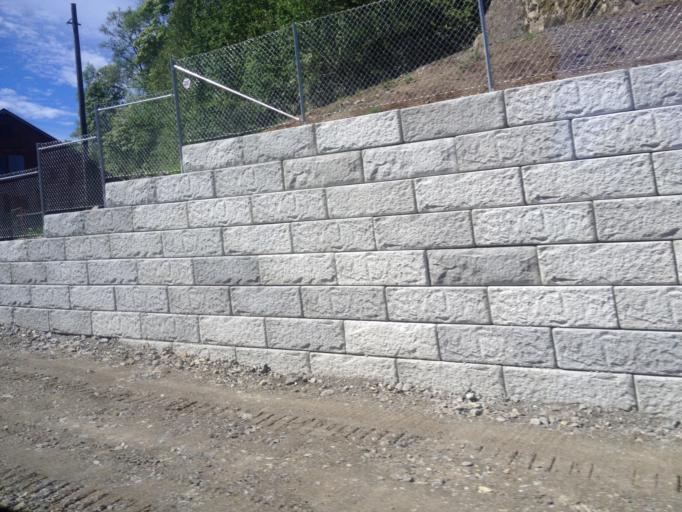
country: NO
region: Rogaland
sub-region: Bjerkreim
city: Vikesa
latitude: 58.5235
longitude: 6.1188
